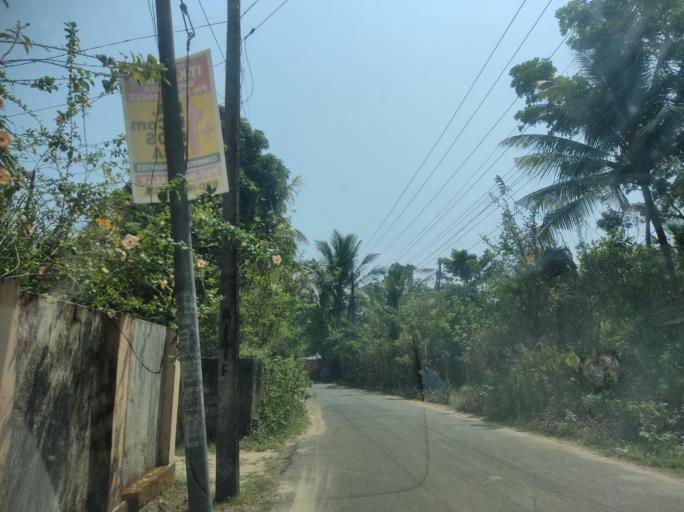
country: IN
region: Kerala
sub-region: Alappuzha
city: Vayalar
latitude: 9.6974
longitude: 76.3030
